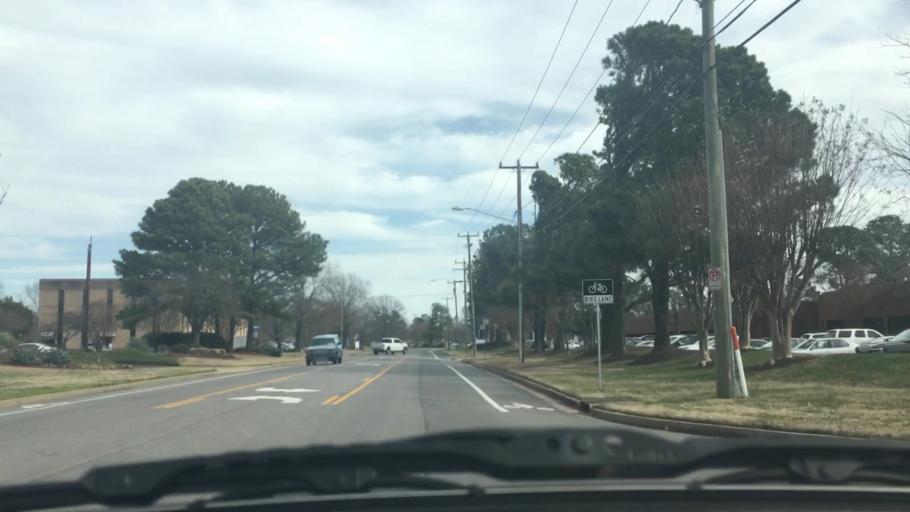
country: US
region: Virginia
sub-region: City of Norfolk
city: Norfolk
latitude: 36.8798
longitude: -76.2224
